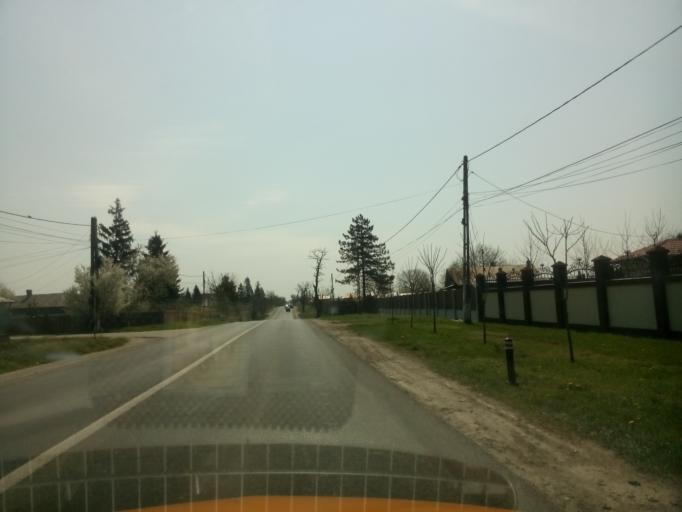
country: RO
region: Calarasi
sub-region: Comuna Frumusani
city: Frumusani
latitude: 44.2996
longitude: 26.3085
